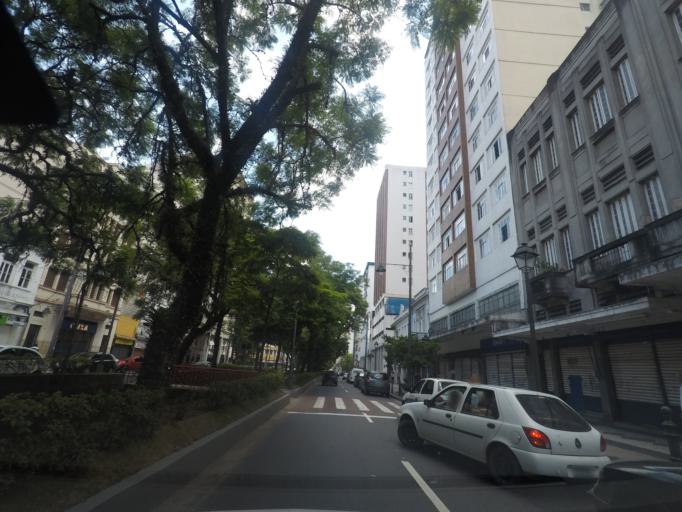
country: BR
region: Rio de Janeiro
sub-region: Petropolis
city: Petropolis
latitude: -22.5080
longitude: -43.1715
